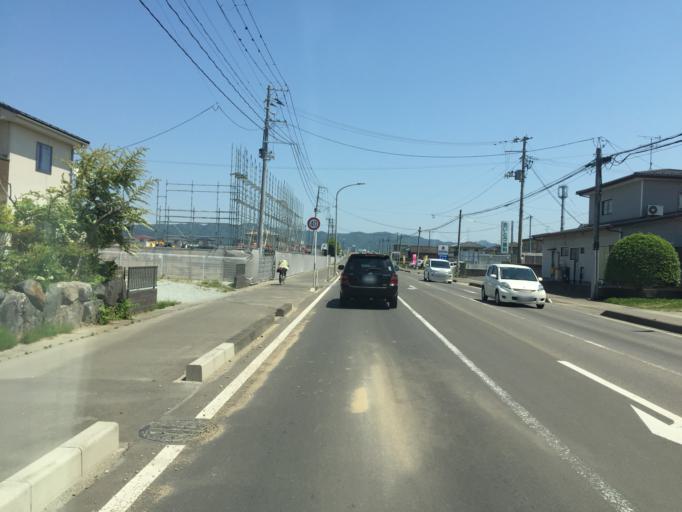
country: JP
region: Miyagi
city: Kakuda
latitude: 37.9753
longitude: 140.7932
